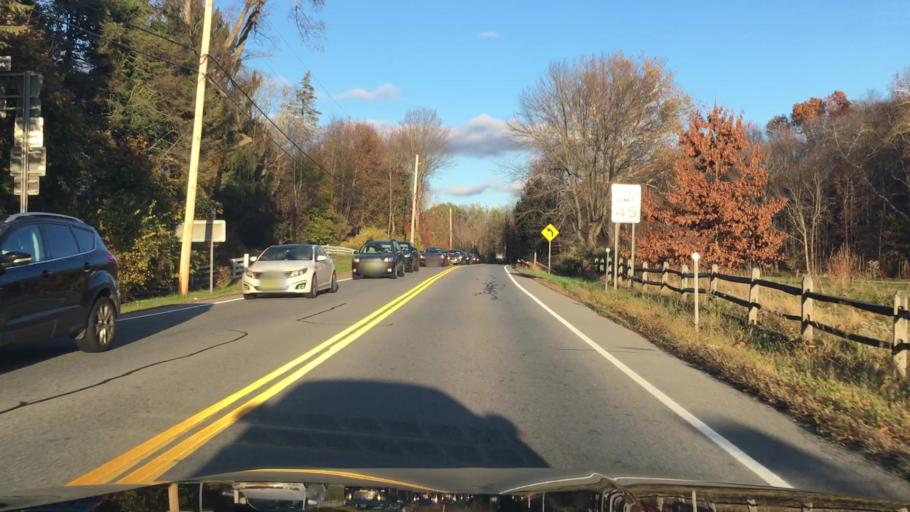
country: US
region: New York
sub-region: Dutchess County
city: Hillside Lake
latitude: 41.6420
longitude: -73.7934
